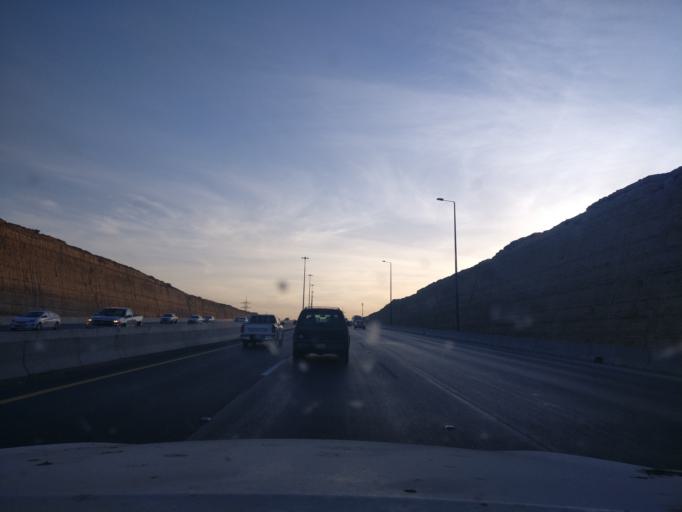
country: SA
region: Ar Riyad
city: Riyadh
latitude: 24.6060
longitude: 46.5584
